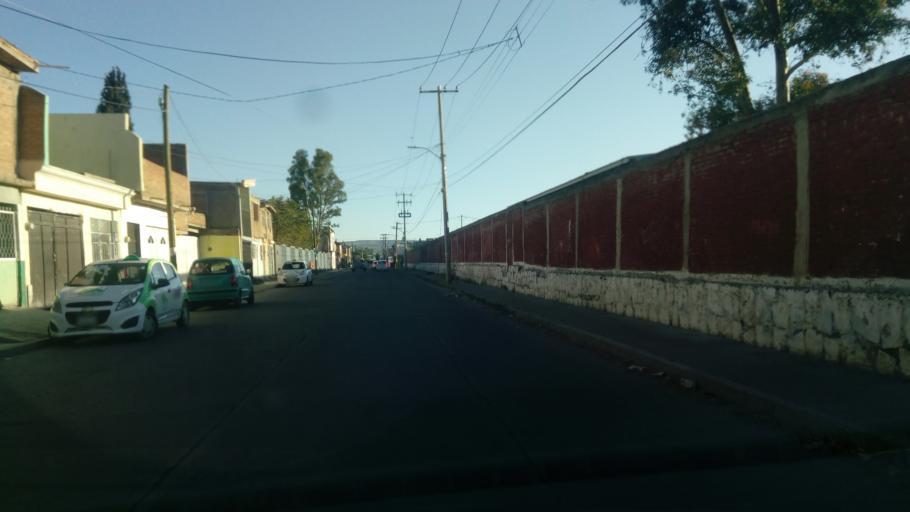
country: MX
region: Durango
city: Victoria de Durango
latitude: 24.0036
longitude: -104.6790
